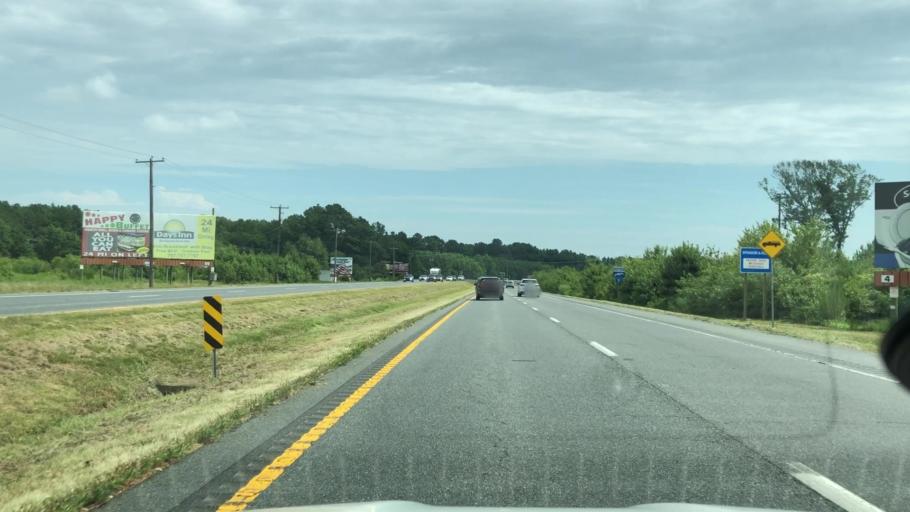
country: US
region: Virginia
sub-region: Accomack County
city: Wattsville
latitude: 37.9872
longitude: -75.5318
